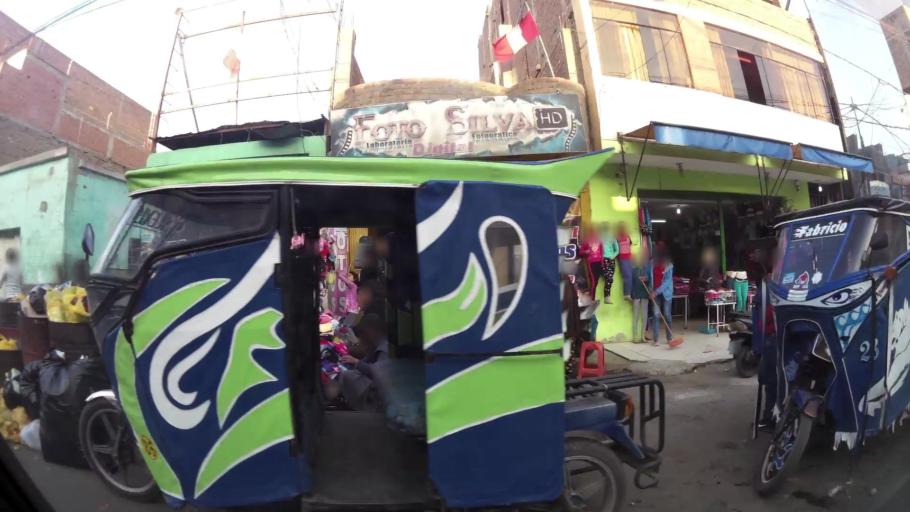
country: PE
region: La Libertad
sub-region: Provincia de Trujillo
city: El Porvenir
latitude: -8.0852
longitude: -79.0016
